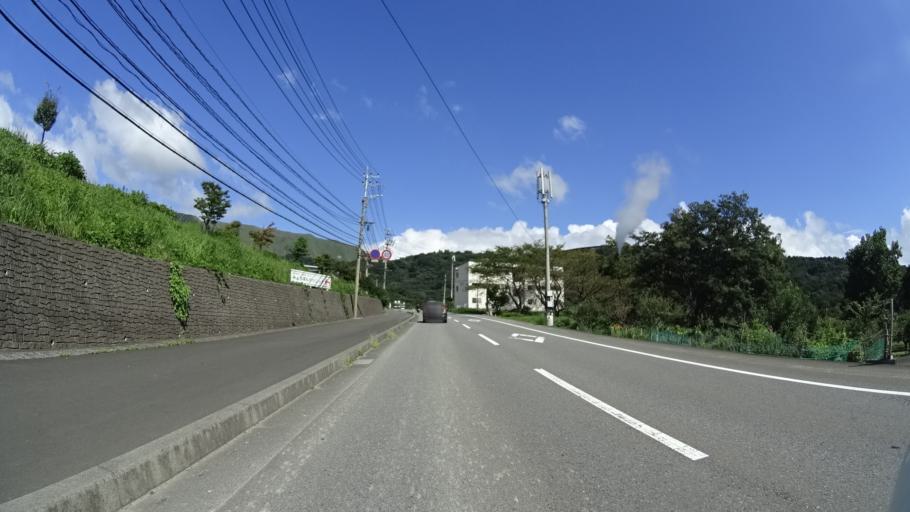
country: JP
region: Oita
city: Beppu
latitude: 33.3126
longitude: 131.4603
